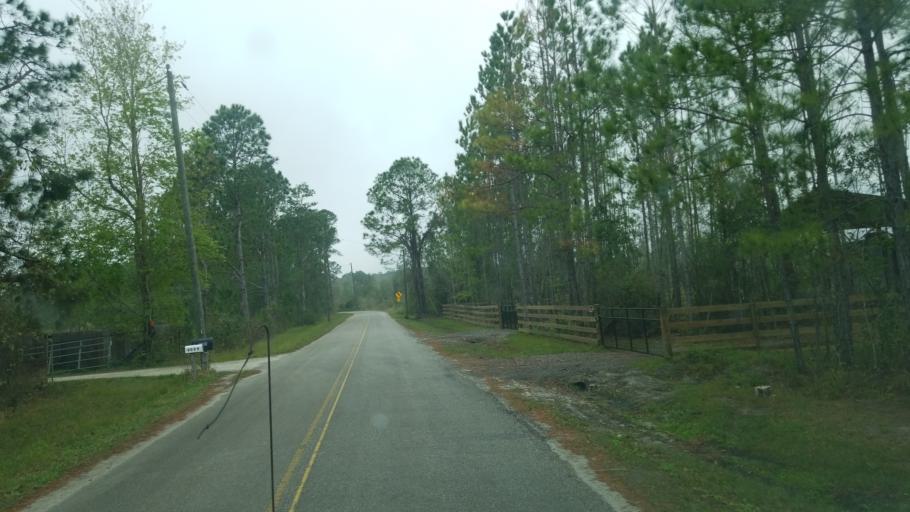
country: US
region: Florida
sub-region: Lake County
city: Groveland
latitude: 28.3875
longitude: -81.8545
